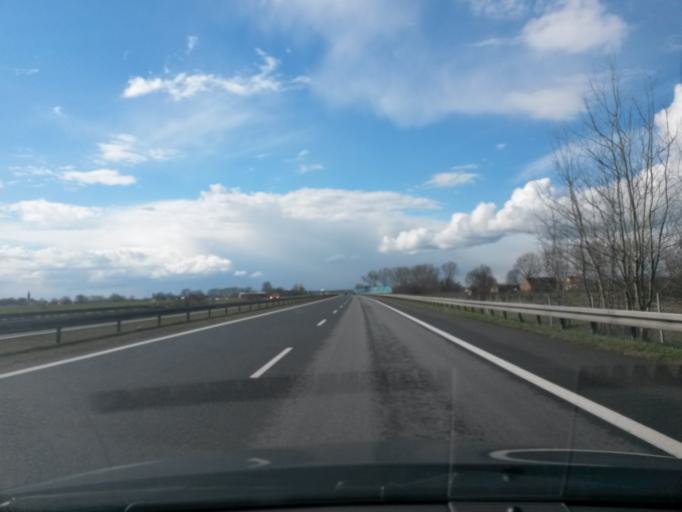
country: PL
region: Greater Poland Voivodeship
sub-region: Powiat wrzesinski
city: Kolaczkowo
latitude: 52.2897
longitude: 17.6699
